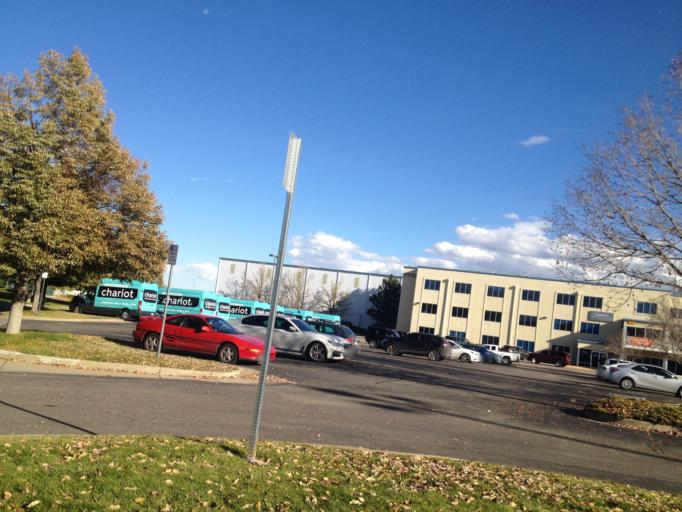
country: US
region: Colorado
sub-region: Broomfield County
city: Broomfield
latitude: 39.9094
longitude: -105.1115
